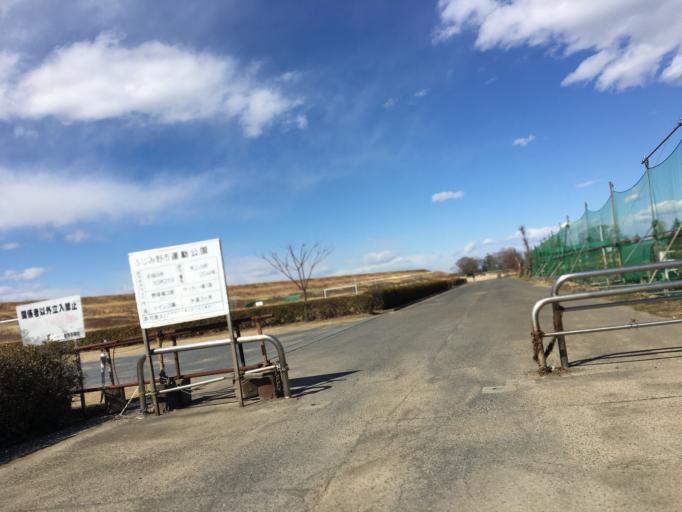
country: JP
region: Saitama
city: Shiki
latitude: 35.8561
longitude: 139.5830
